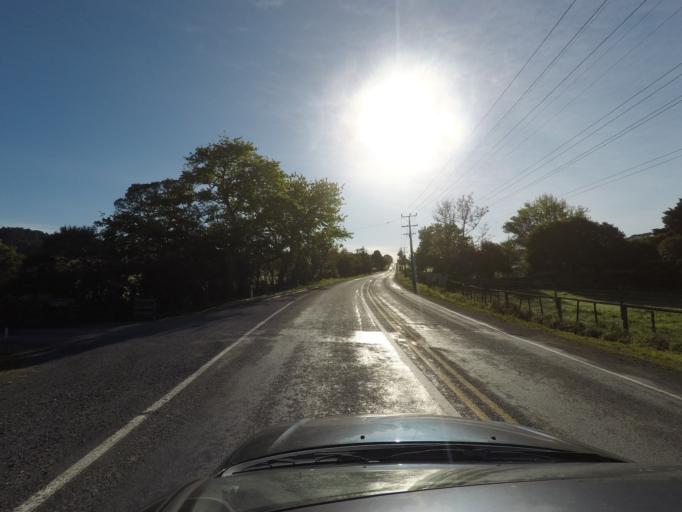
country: NZ
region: Auckland
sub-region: Auckland
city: Red Hill
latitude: -36.9985
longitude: 174.9685
